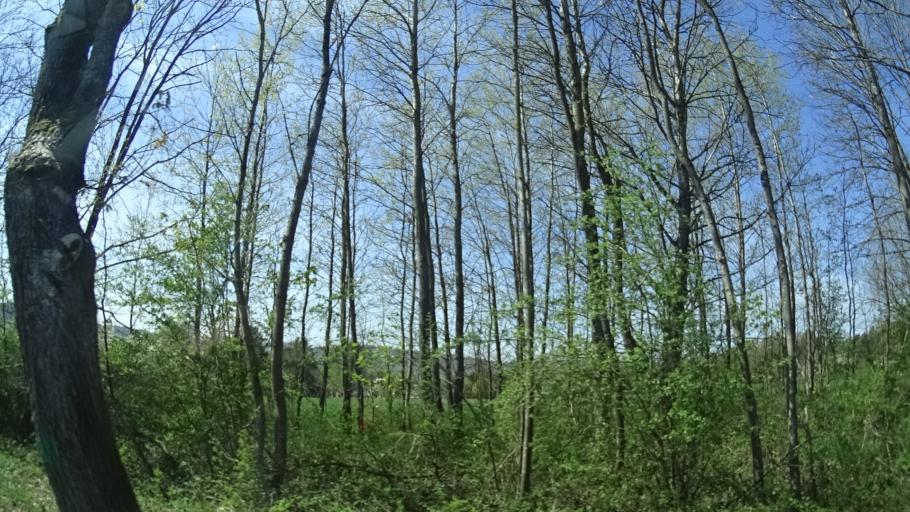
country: DE
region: Thuringia
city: Hildburghausen
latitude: 50.4362
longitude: 10.7479
